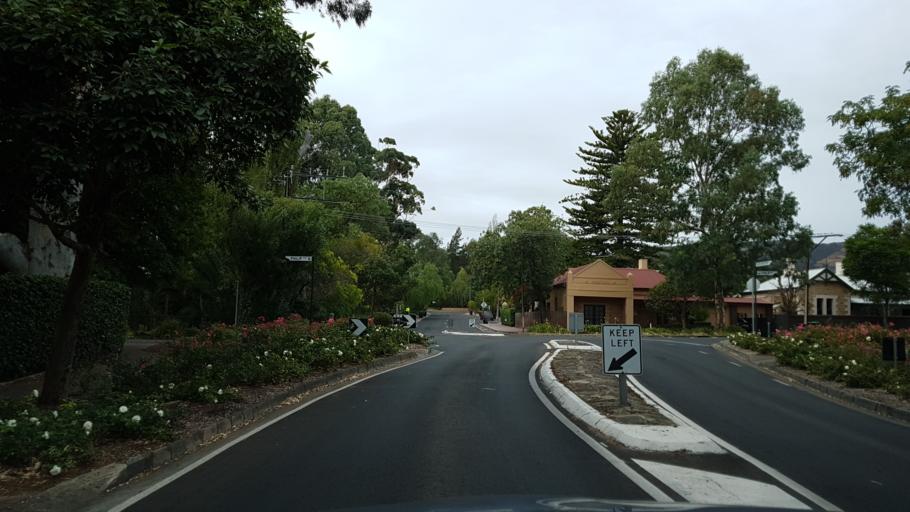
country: AU
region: South Australia
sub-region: Burnside
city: Leabrook
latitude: -34.9315
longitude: 138.6559
